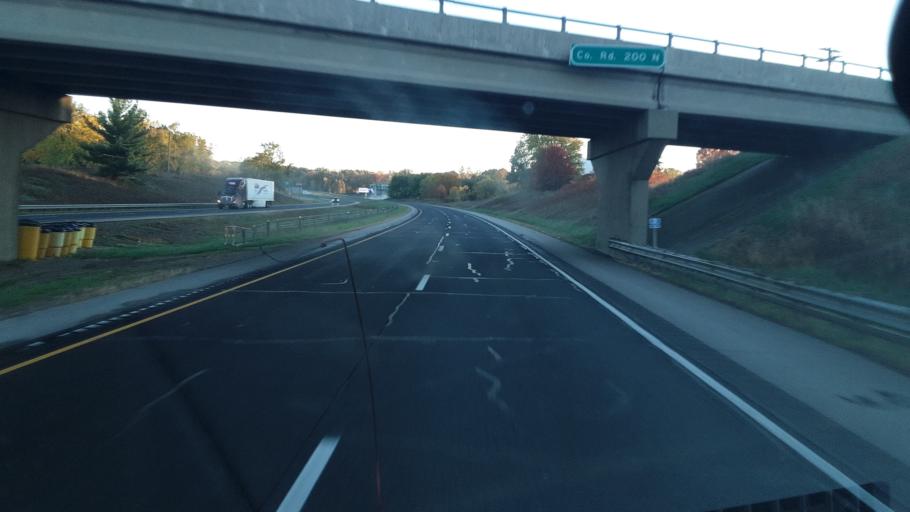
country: US
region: Indiana
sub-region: Steuben County
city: Angola
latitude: 41.6710
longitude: -85.0100
